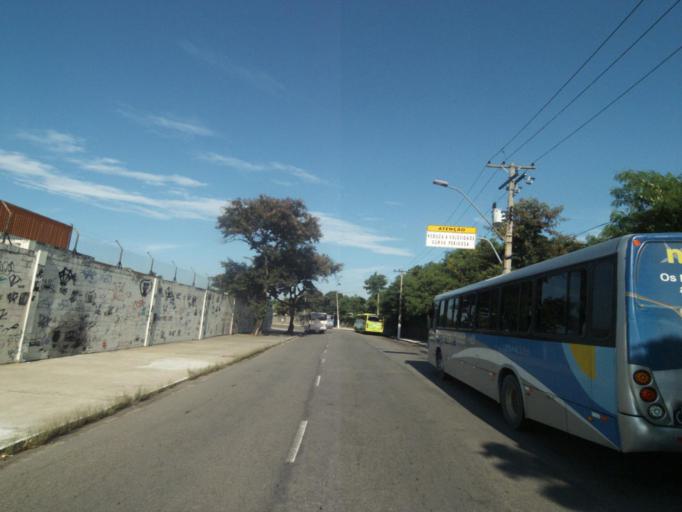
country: BR
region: Rio de Janeiro
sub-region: Niteroi
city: Niteroi
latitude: -22.8860
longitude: -43.1266
